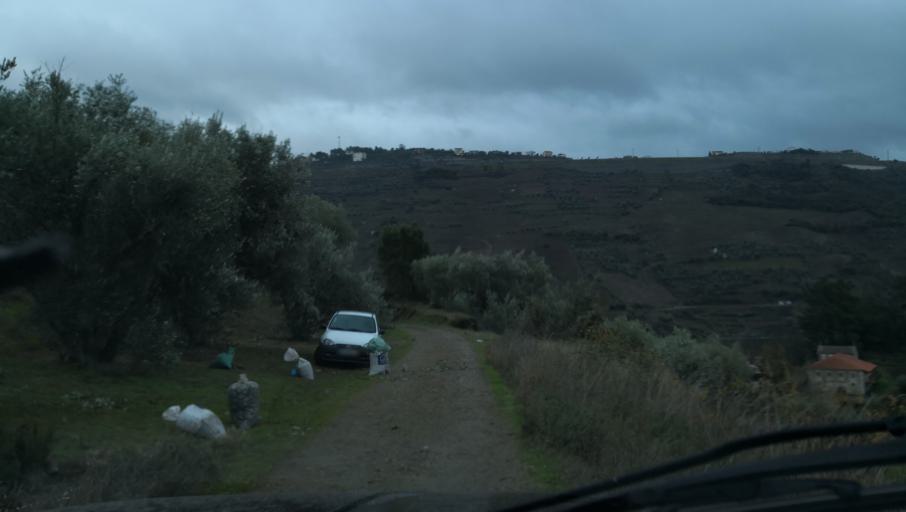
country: PT
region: Vila Real
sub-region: Santa Marta de Penaguiao
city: Santa Marta de Penaguiao
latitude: 41.2366
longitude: -7.7447
